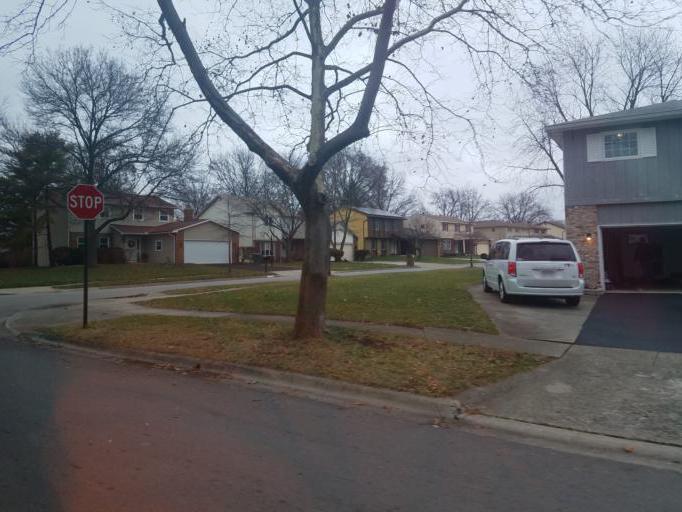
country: US
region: Ohio
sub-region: Franklin County
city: Minerva Park
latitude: 40.0960
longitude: -82.9461
